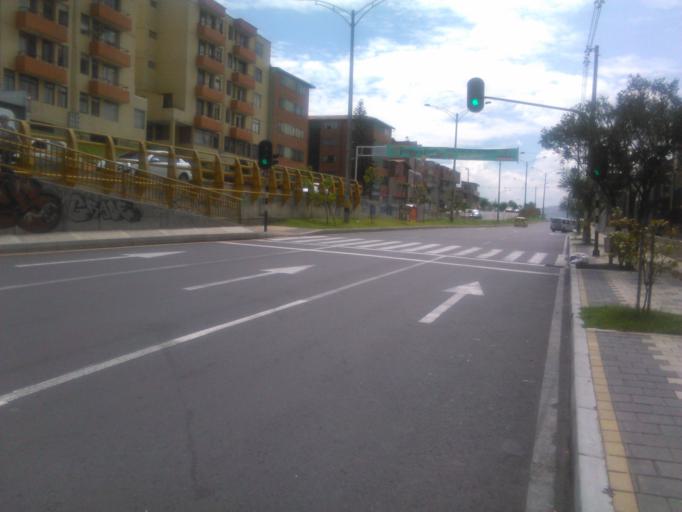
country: CO
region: Antioquia
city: Medellin
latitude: 6.2821
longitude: -75.5855
